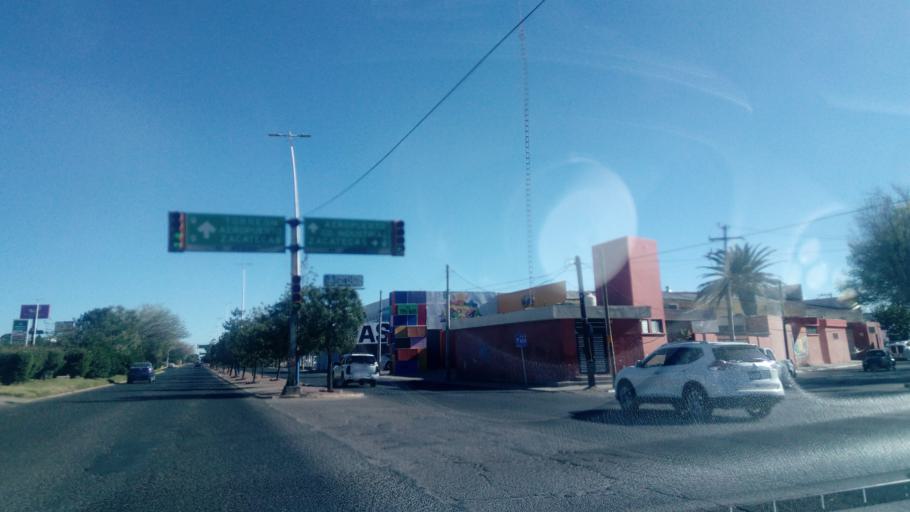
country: MX
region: Durango
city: Victoria de Durango
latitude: 24.0451
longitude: -104.6255
